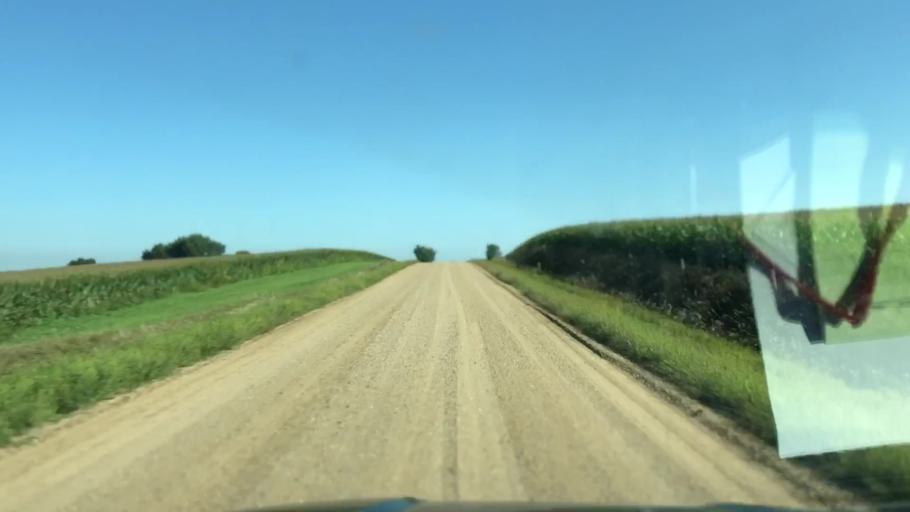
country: US
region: Iowa
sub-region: Woodbury County
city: Sergeant Bluff
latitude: 42.4349
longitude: -96.2923
